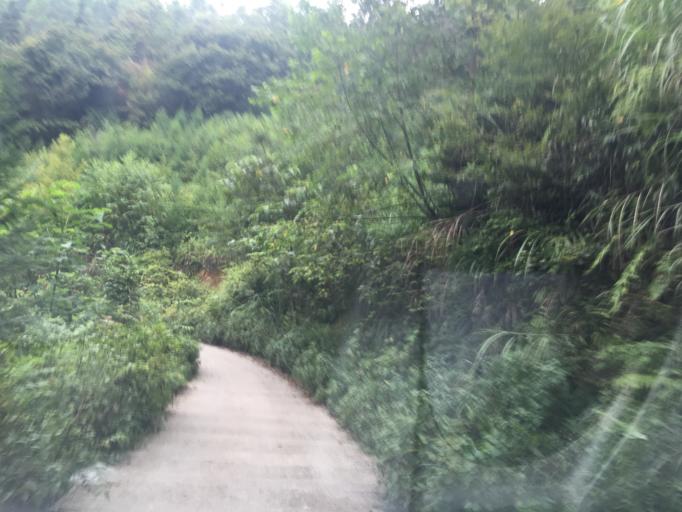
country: CN
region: Guangxi Zhuangzu Zizhiqu
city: Xinzhou
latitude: 25.1597
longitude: 105.6999
